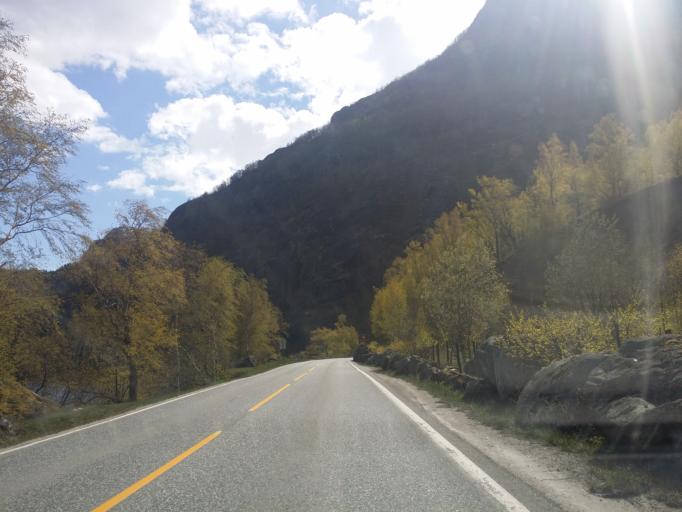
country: NO
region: Hordaland
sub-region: Eidfjord
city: Eidfjord
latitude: 60.4558
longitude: 7.0926
